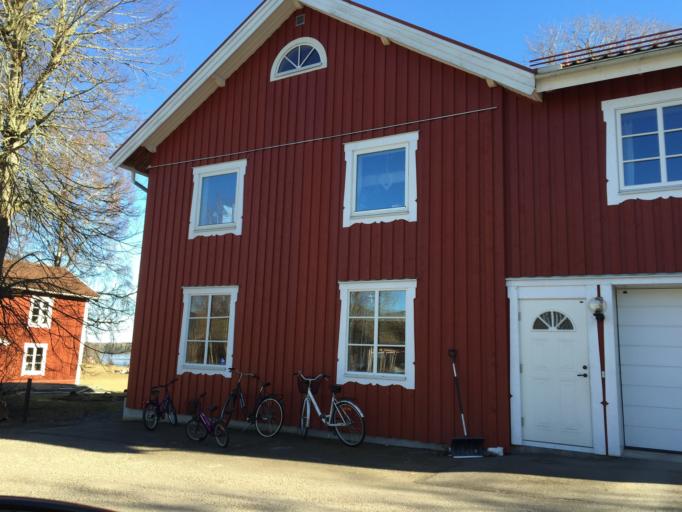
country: SE
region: Soedermanland
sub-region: Vingakers Kommun
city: Vingaker
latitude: 58.9835
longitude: 15.8072
